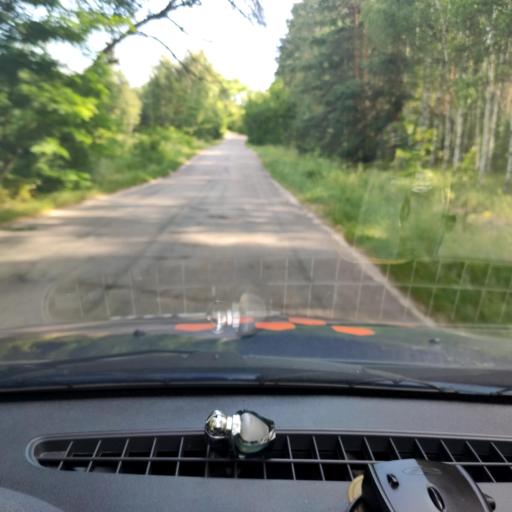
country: RU
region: Voronezj
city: Somovo
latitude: 51.7828
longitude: 39.4054
